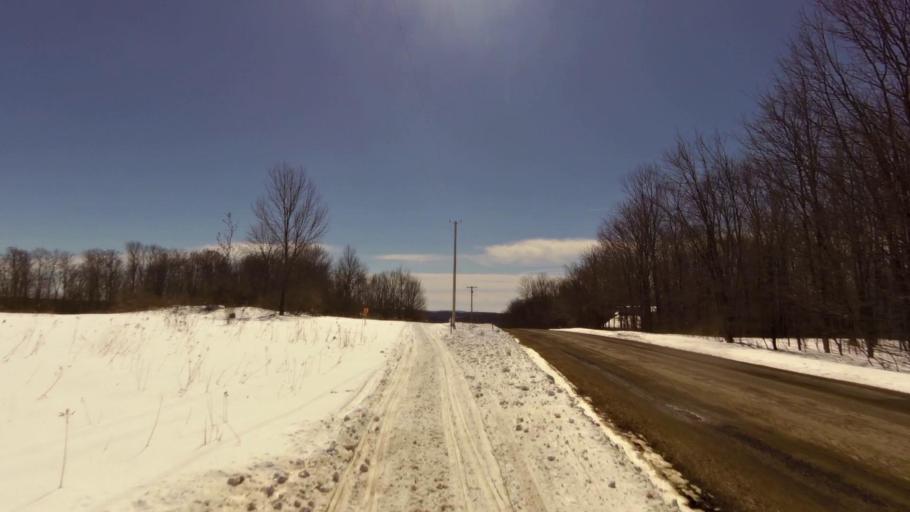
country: US
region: New York
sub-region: Allegany County
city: Houghton
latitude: 42.3506
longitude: -78.2604
